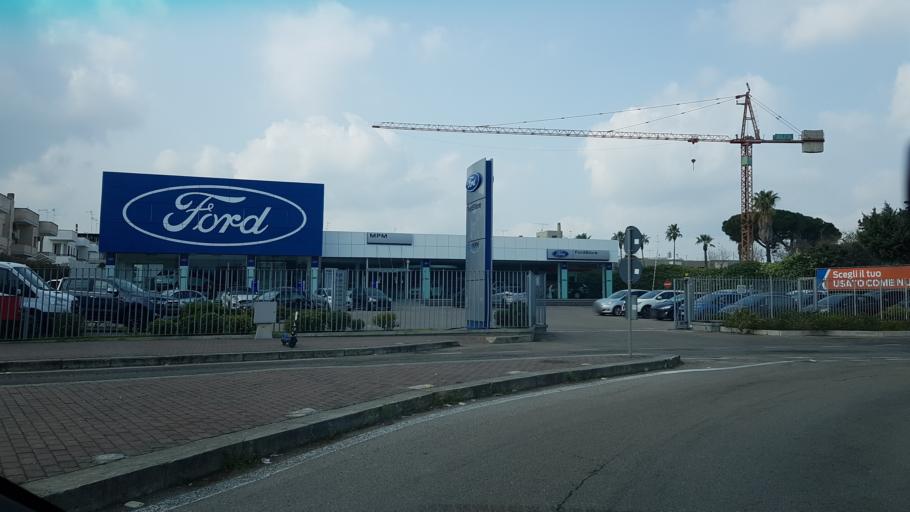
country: IT
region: Apulia
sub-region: Provincia di Lecce
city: Castromediano
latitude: 40.3305
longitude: 18.1811
